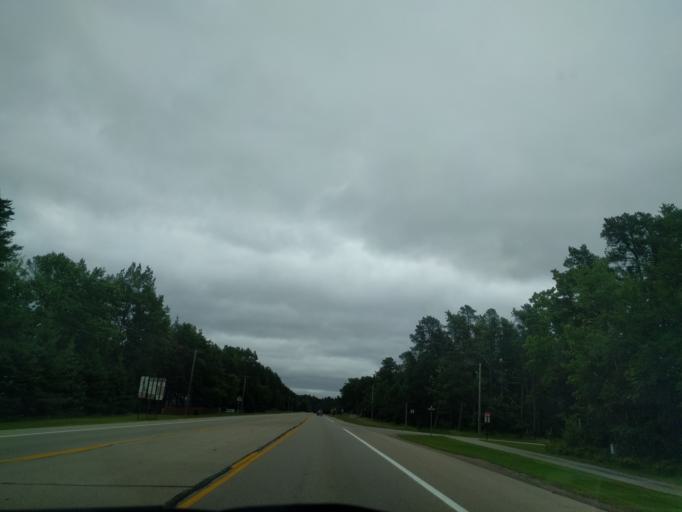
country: US
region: Michigan
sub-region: Delta County
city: Gladstone
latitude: 45.8555
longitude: -87.0451
